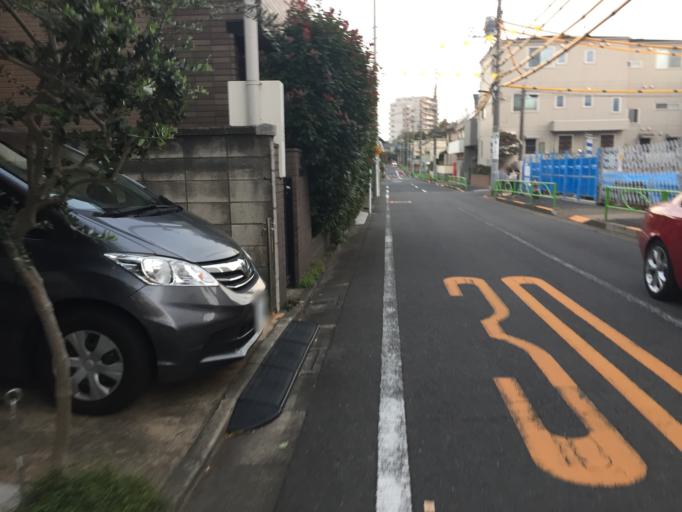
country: JP
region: Tokyo
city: Tokyo
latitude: 35.6308
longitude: 139.6649
